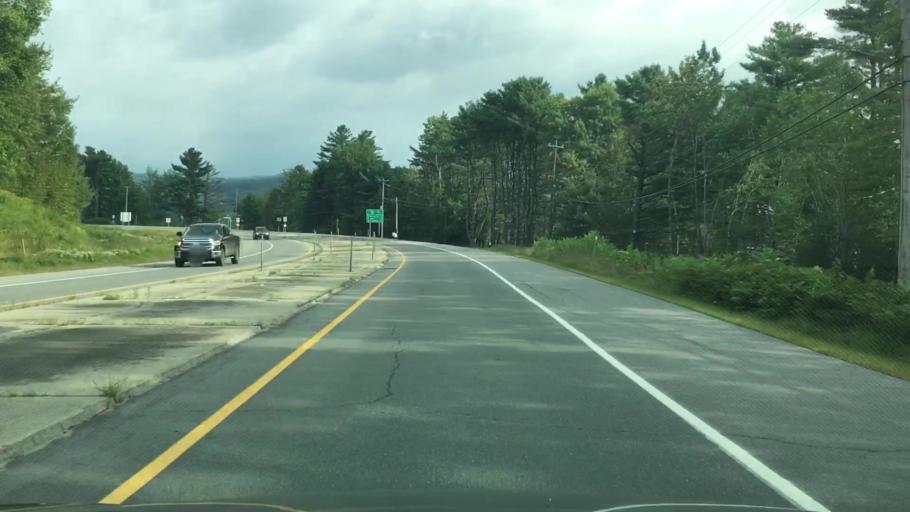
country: US
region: New Hampshire
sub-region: Grafton County
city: Littleton
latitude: 44.3306
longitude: -71.8741
